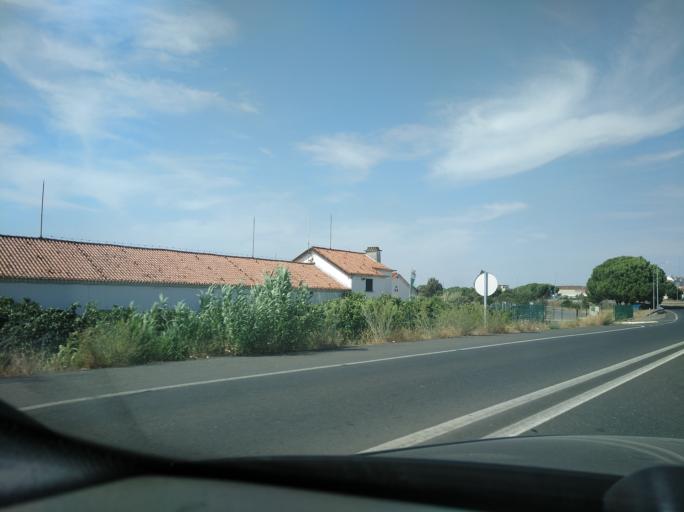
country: PT
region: Beja
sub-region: Beja
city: Beja
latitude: 38.0007
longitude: -7.8664
